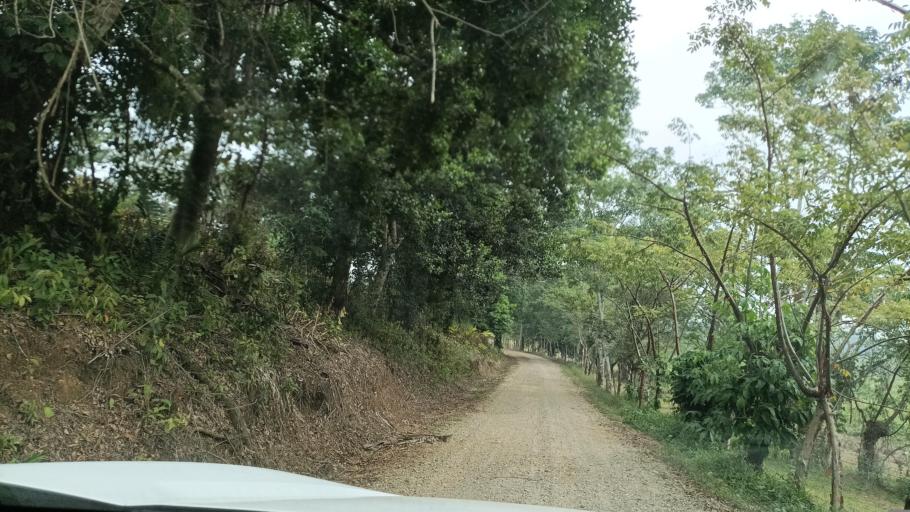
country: MX
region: Veracruz
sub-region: Uxpanapa
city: Poblado 10
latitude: 17.5451
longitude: -94.2349
